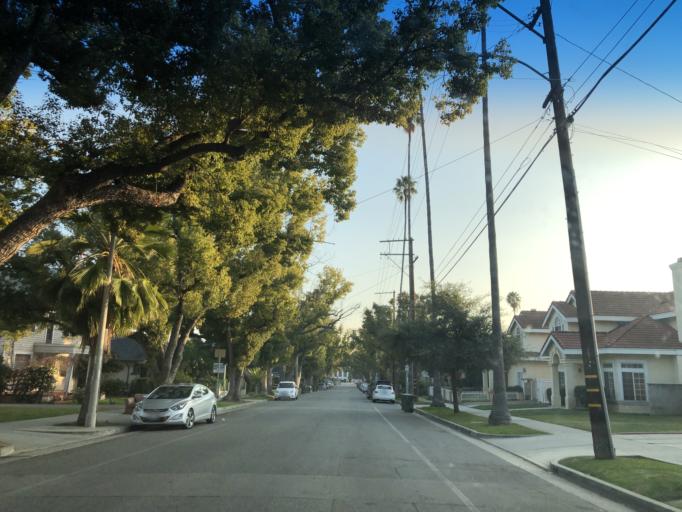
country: US
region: California
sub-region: Los Angeles County
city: East Pasadena
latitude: 34.1487
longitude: -118.1171
